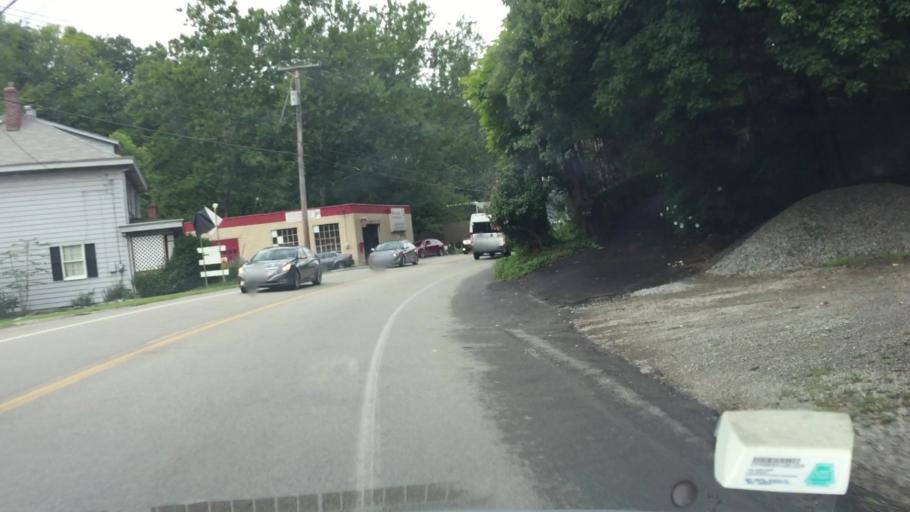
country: US
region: Pennsylvania
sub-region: Allegheny County
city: Millvale
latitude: 40.5018
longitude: -79.9844
